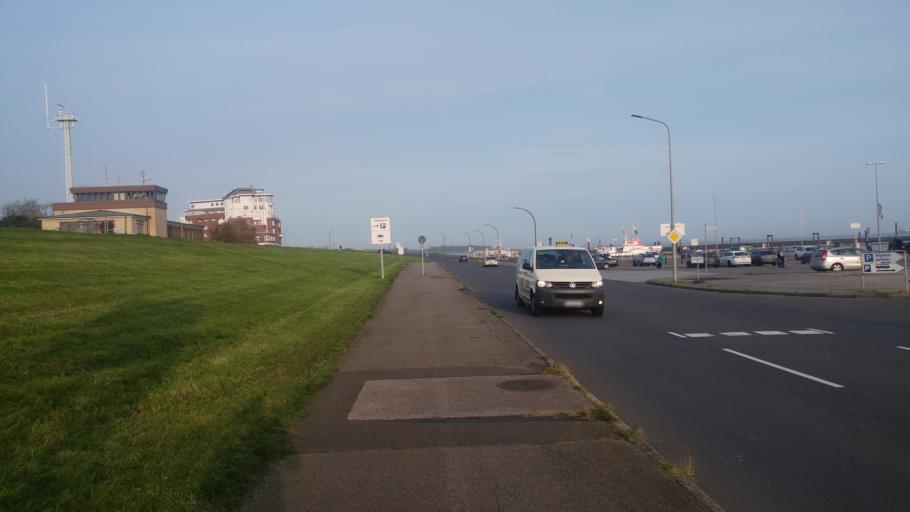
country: DE
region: Lower Saxony
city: Cuxhaven
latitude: 53.8742
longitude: 8.6998
